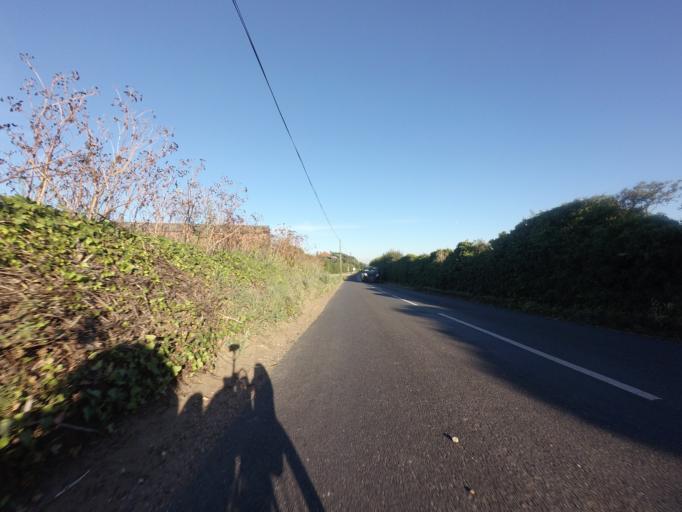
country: GB
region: England
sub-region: Kent
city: Herne Bay
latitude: 51.3495
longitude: 1.1831
